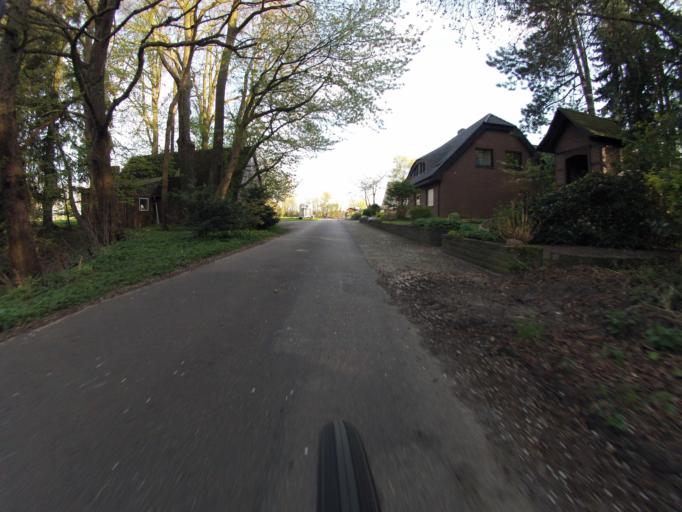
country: DE
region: Lower Saxony
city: Salzbergen
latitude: 52.3364
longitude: 7.3581
